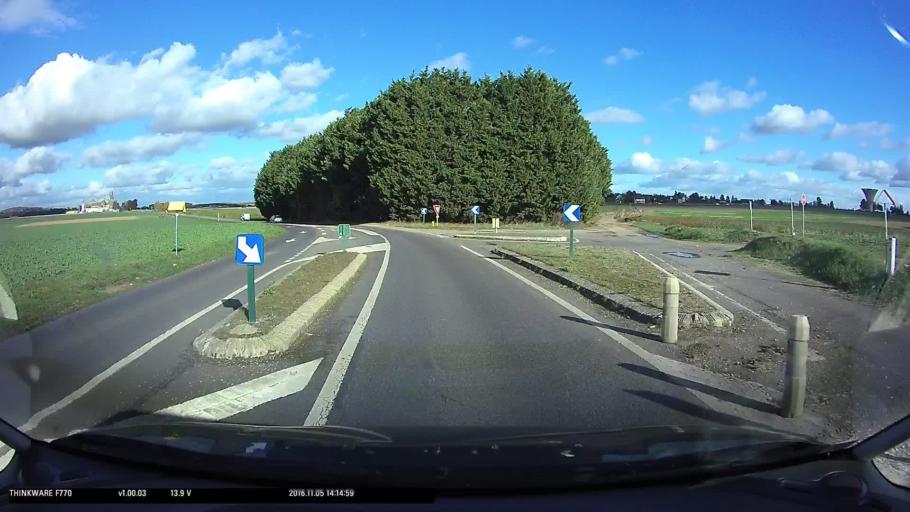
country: FR
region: Ile-de-France
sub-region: Departement du Val-d'Oise
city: Osny
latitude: 49.0850
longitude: 2.0552
